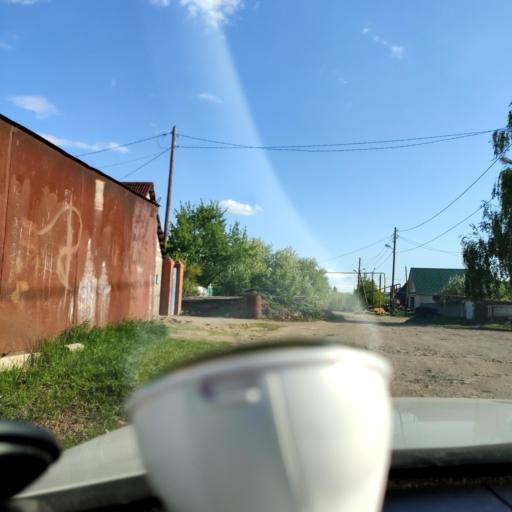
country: RU
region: Samara
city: Petra-Dubrava
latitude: 53.2591
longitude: 50.3444
